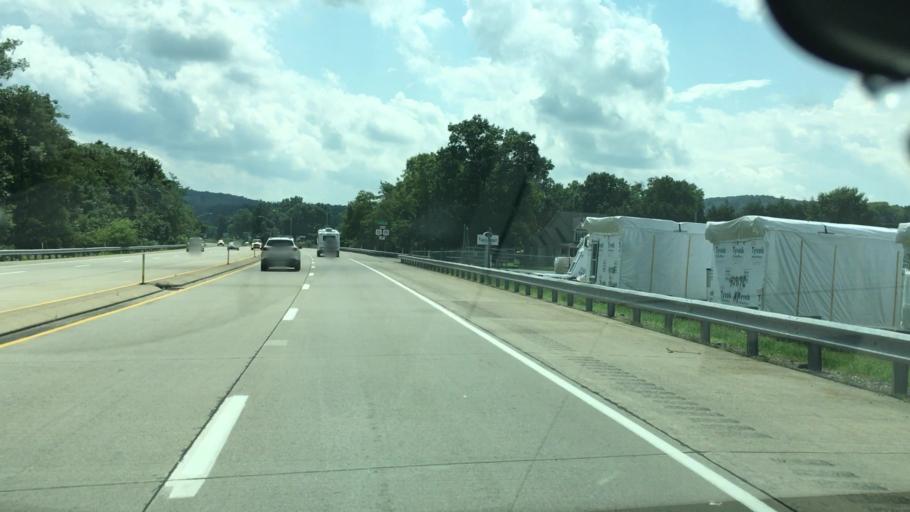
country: US
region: Pennsylvania
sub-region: Dauphin County
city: Millersburg
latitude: 40.6376
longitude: -76.9461
